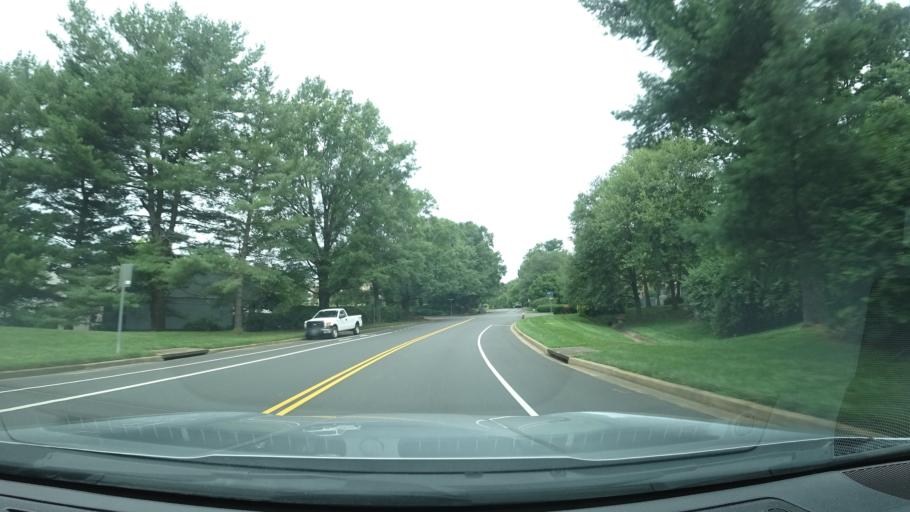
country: US
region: Virginia
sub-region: Fairfax County
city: Reston
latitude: 38.9560
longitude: -77.3417
